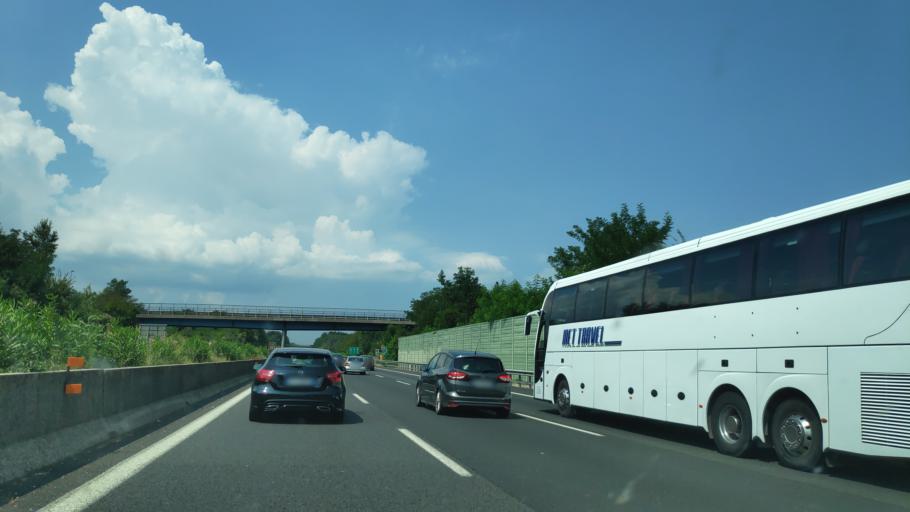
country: IT
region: Latium
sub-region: Citta metropolitana di Roma Capitale
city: Valmontone
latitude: 41.7690
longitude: 12.9119
